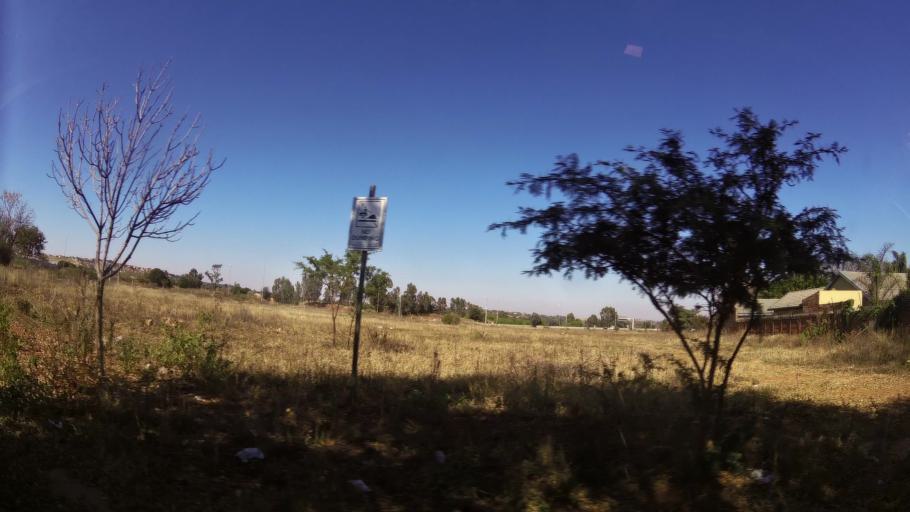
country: ZA
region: Gauteng
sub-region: City of Tshwane Metropolitan Municipality
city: Centurion
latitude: -25.8316
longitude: 28.2392
